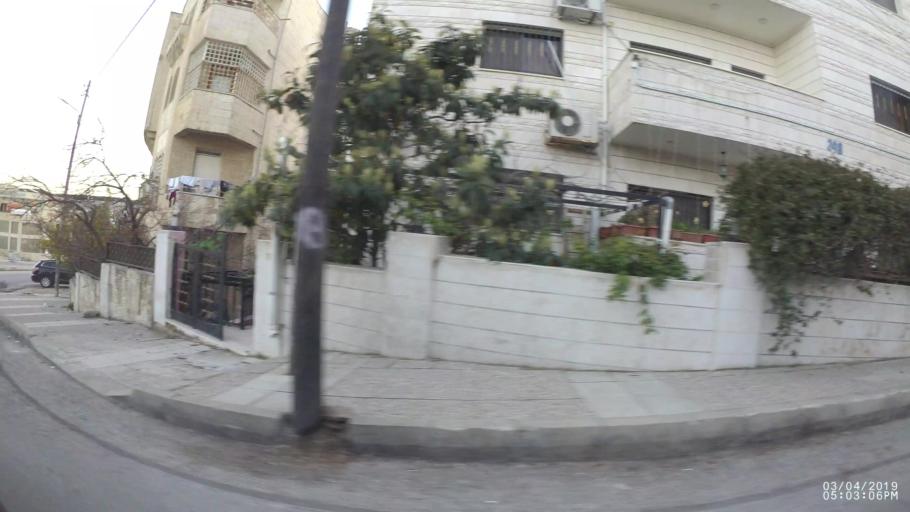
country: JO
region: Amman
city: Al Bunayyat ash Shamaliyah
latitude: 31.9189
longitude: 35.8970
